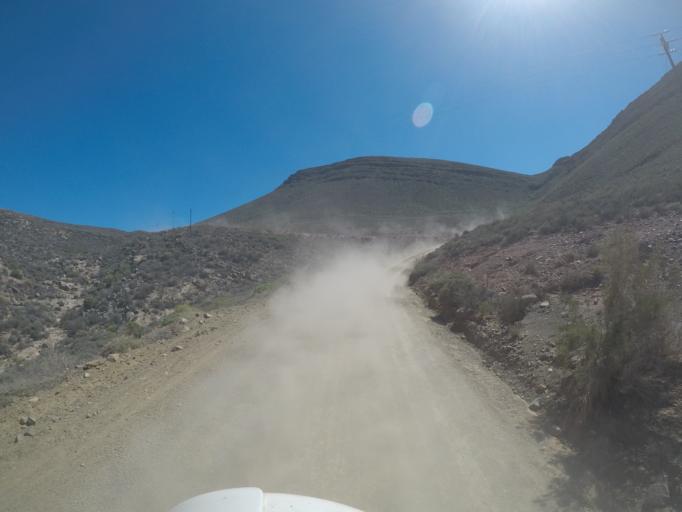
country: ZA
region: Western Cape
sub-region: West Coast District Municipality
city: Clanwilliam
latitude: -32.6158
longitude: 19.3749
